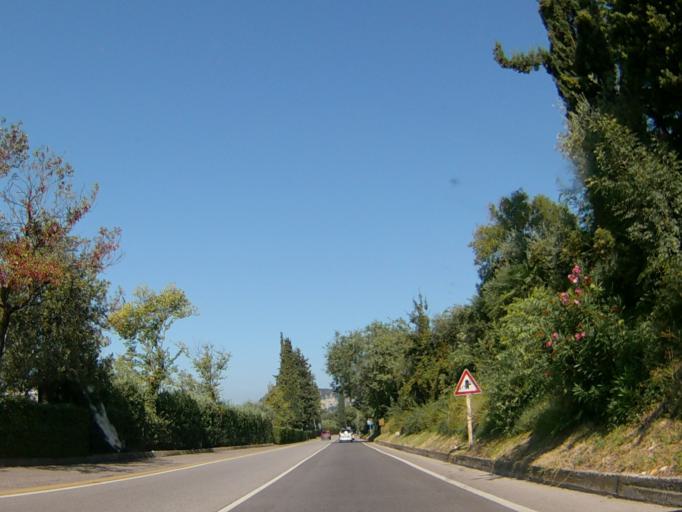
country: IT
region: Veneto
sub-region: Provincia di Verona
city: Garda
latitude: 45.5649
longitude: 10.7128
